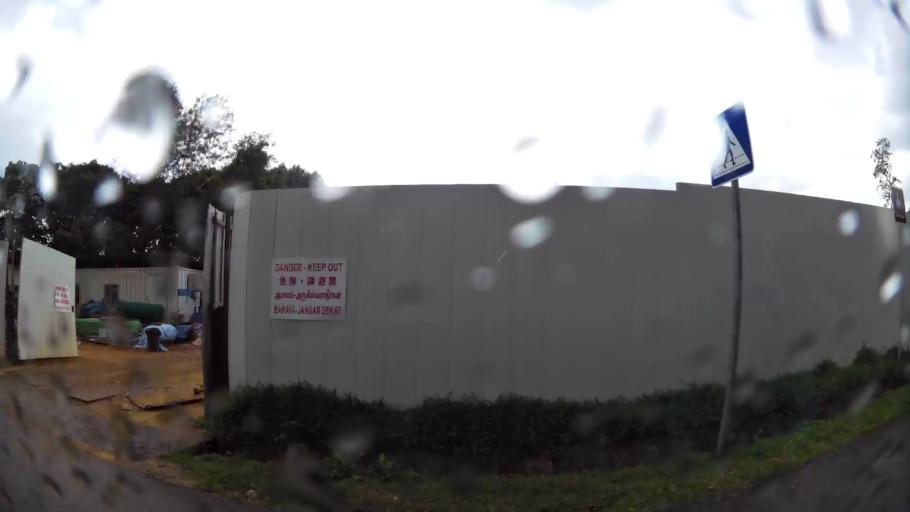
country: MY
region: Johor
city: Kampung Pasir Gudang Baru
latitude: 1.4093
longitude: 103.8667
